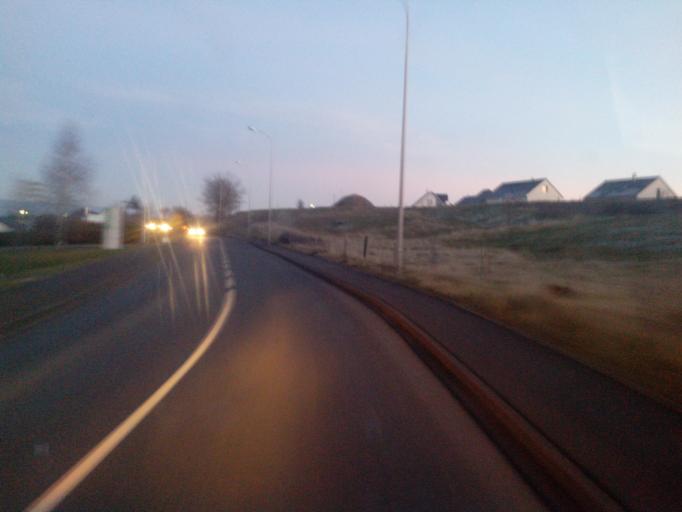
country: FR
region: Auvergne
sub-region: Departement du Cantal
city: Saint-Flour
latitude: 45.0376
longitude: 3.0741
